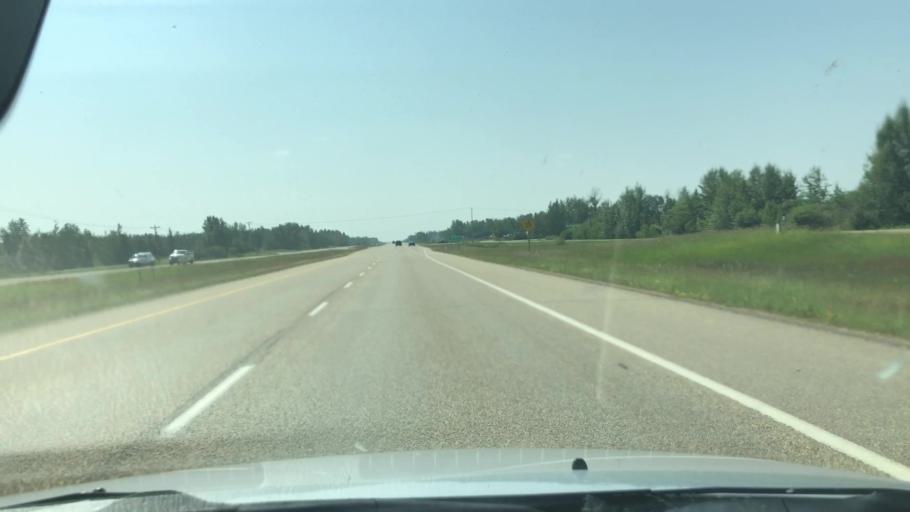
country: CA
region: Alberta
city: Devon
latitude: 53.4281
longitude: -113.7635
